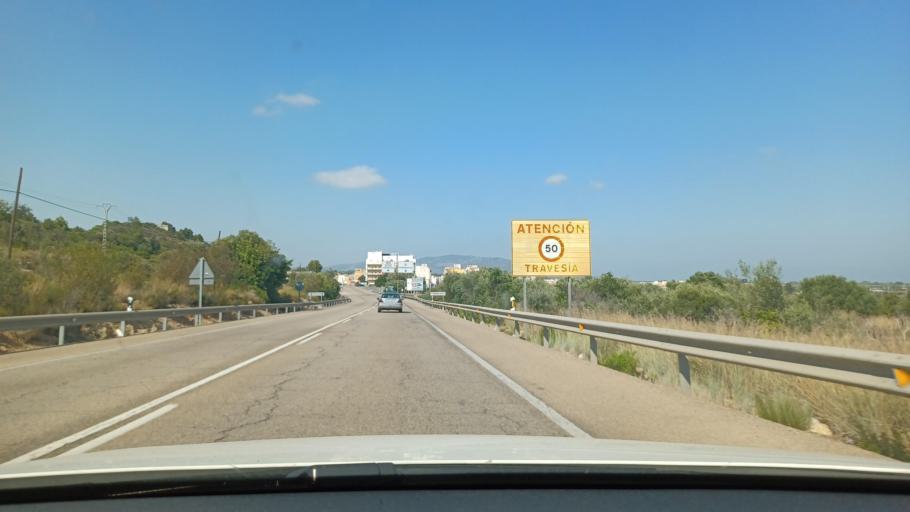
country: ES
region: Valencia
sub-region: Provincia de Castello
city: Torreblanca
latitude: 40.2129
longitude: 0.1840
